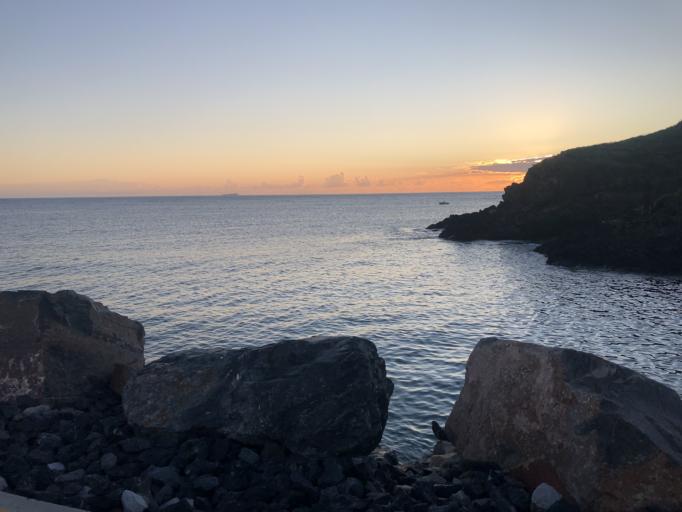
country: AU
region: New South Wales
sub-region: Coffs Harbour
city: Coffs Harbour
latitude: -30.3046
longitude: 153.1483
